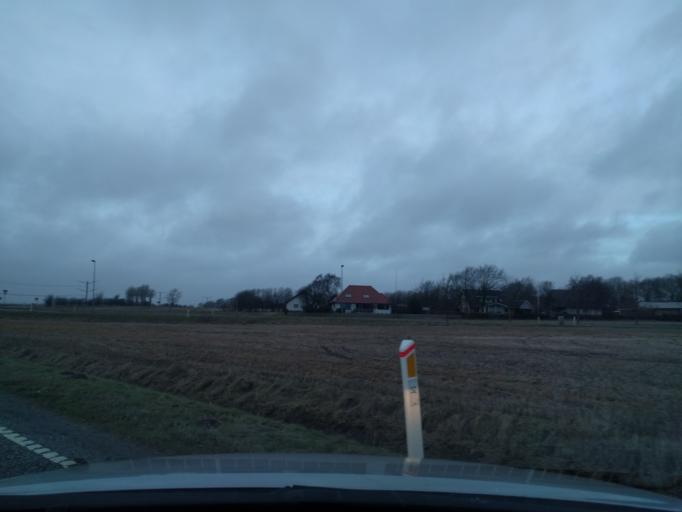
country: DK
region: South Denmark
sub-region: Tonder Kommune
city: Toftlund
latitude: 55.2533
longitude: 9.1471
